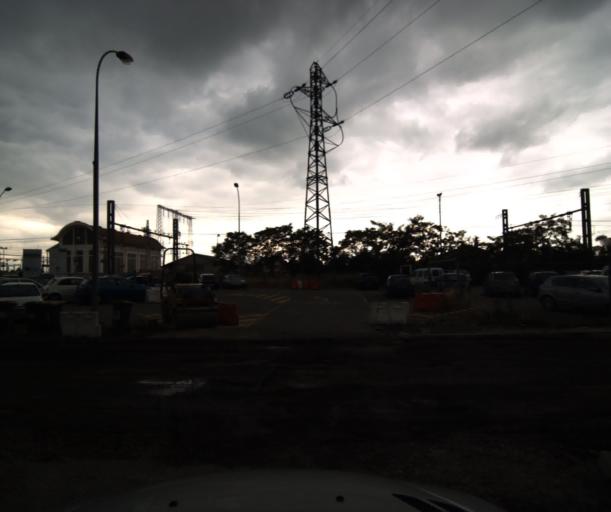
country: FR
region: Midi-Pyrenees
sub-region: Departement de la Haute-Garonne
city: Portet-sur-Garonne
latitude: 43.5283
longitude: 1.3901
